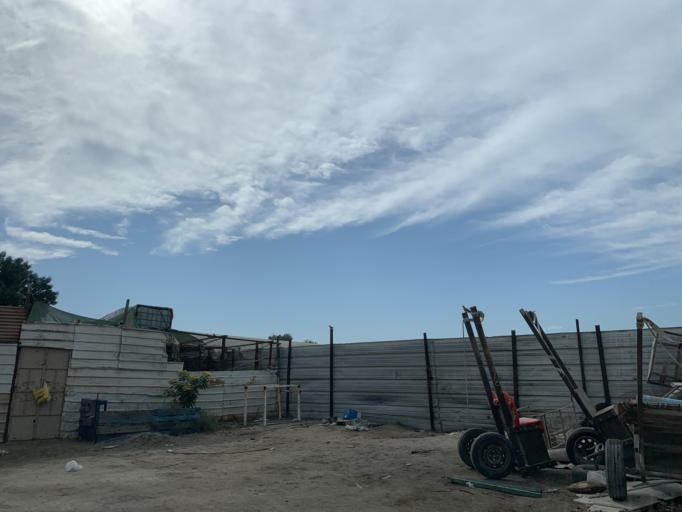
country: BH
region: Central Governorate
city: Madinat Hamad
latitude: 26.1128
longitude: 50.4784
